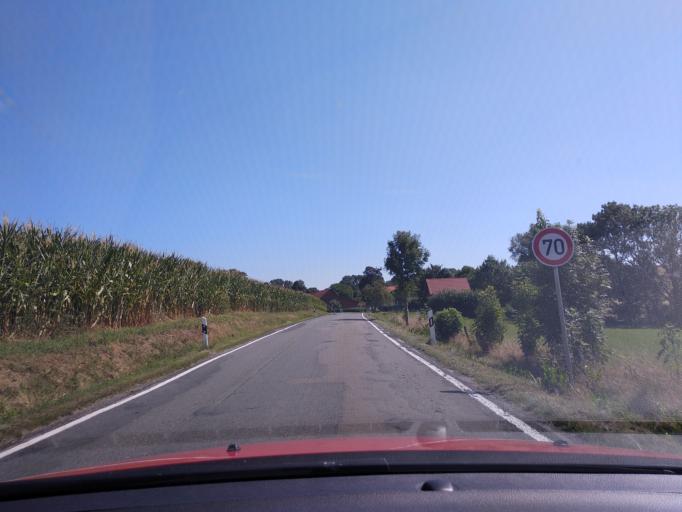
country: DE
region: North Rhine-Westphalia
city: Brakel
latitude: 51.6423
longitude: 9.1852
